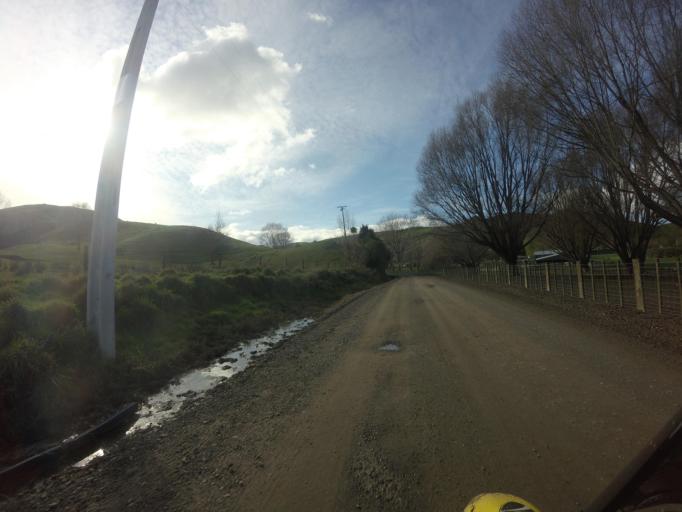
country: NZ
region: Hawke's Bay
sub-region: Wairoa District
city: Wairoa
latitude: -38.9913
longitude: 177.5931
